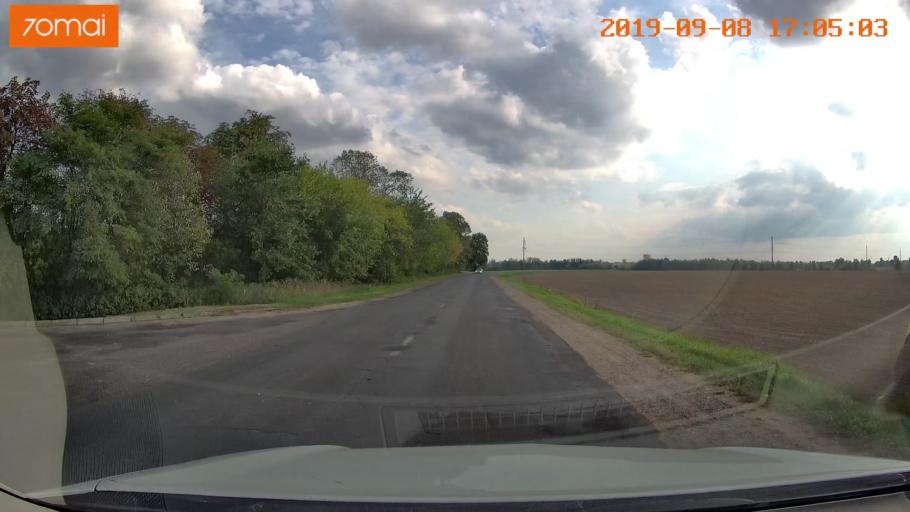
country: BY
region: Grodnenskaya
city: Hrodna
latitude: 53.6828
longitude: 23.9559
